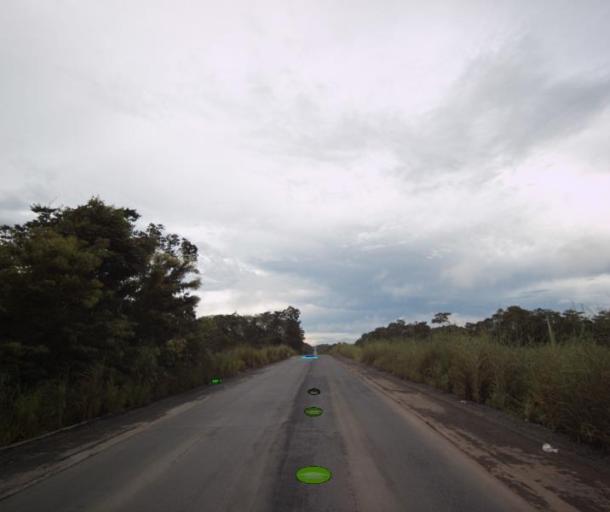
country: BR
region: Goias
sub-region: Porangatu
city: Porangatu
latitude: -13.5519
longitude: -49.0932
